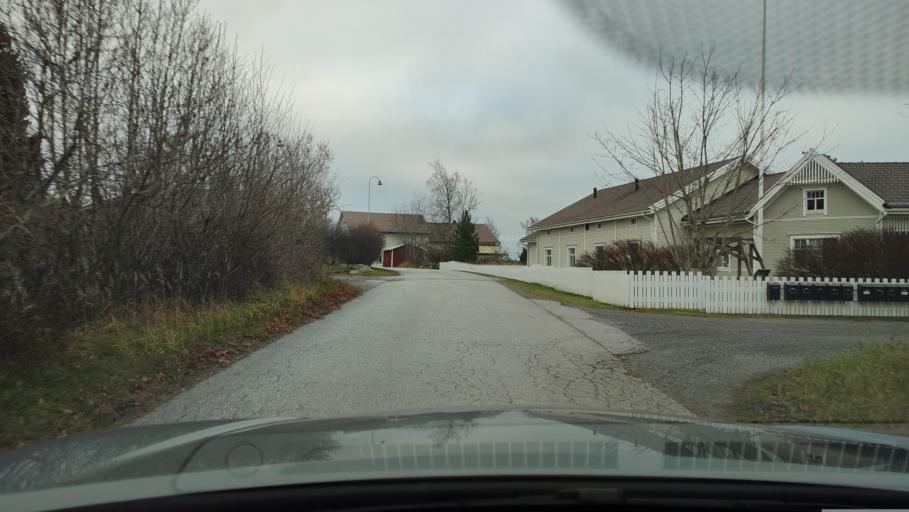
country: FI
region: Ostrobothnia
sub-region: Sydosterbotten
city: Kristinestad
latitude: 62.2699
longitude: 21.3708
